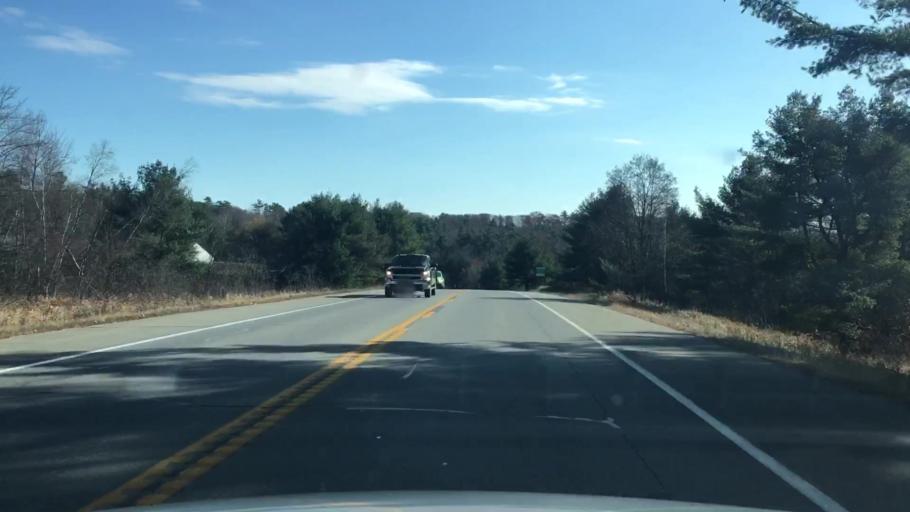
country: US
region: Maine
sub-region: Kennebec County
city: Windsor
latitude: 44.2602
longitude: -69.5565
